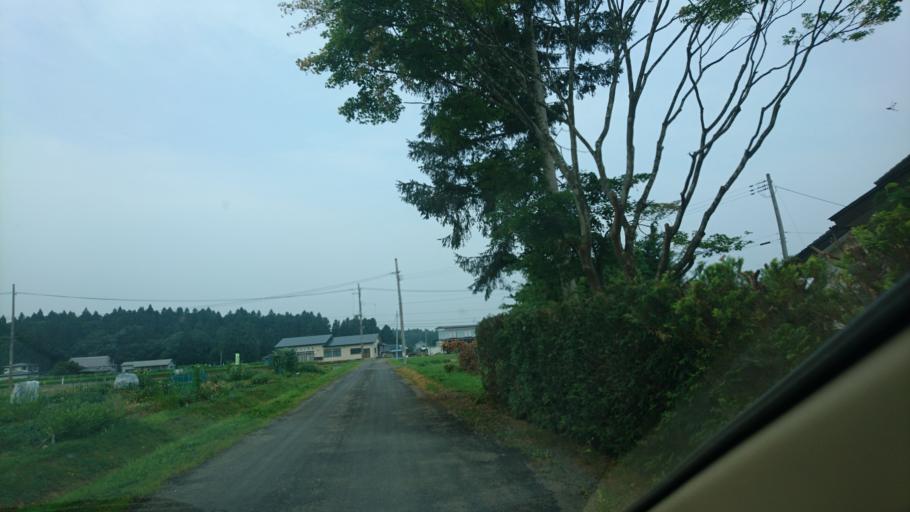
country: JP
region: Iwate
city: Kitakami
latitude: 39.2475
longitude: 141.0849
